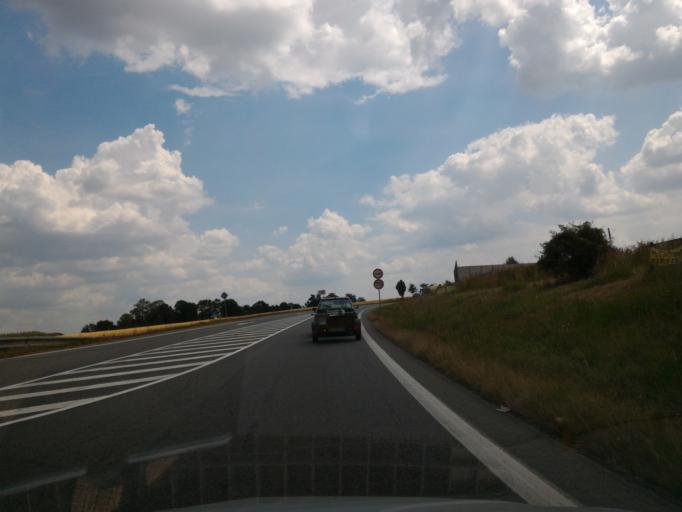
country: CZ
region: Vysocina
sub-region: Okres Havlickuv Brod
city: Havlickuv Brod
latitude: 49.6138
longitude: 15.5893
